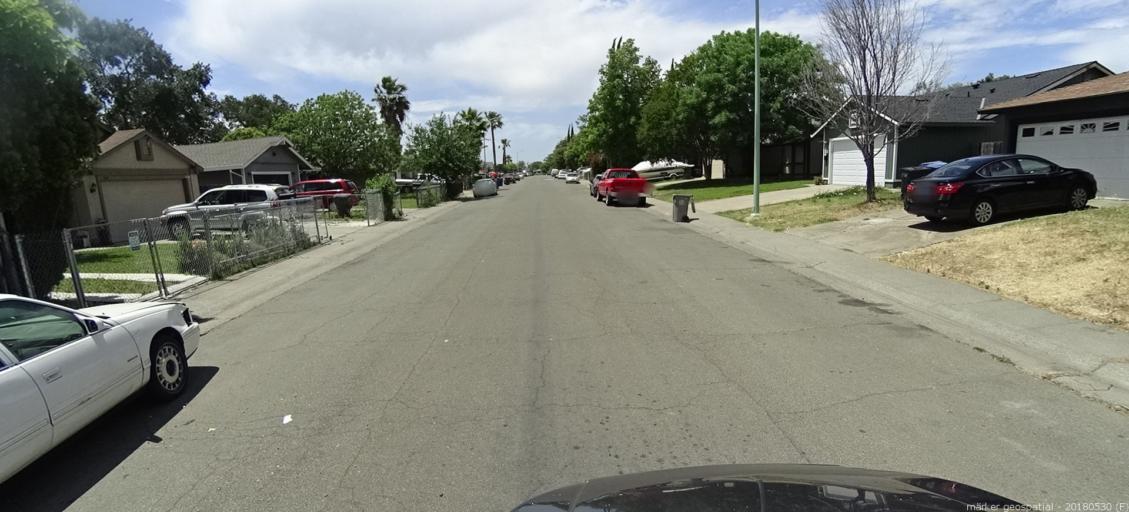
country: US
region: California
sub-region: Sacramento County
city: Sacramento
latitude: 38.6279
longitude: -121.4595
